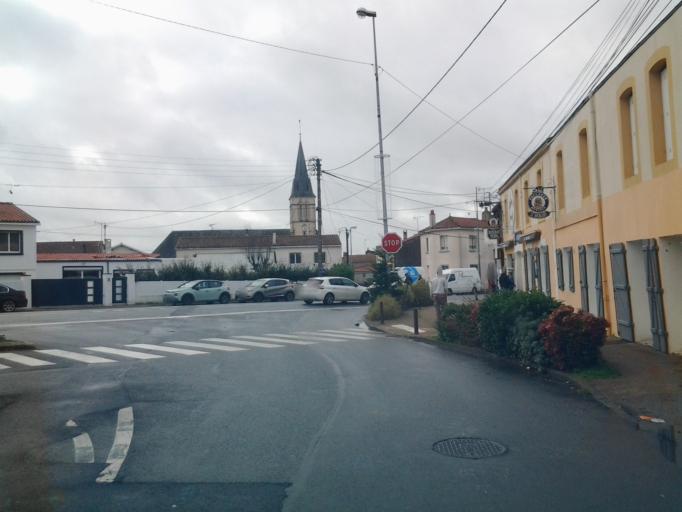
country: FR
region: Pays de la Loire
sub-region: Departement de la Vendee
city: La Roche-sur-Yon
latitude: 46.6615
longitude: -1.4006
